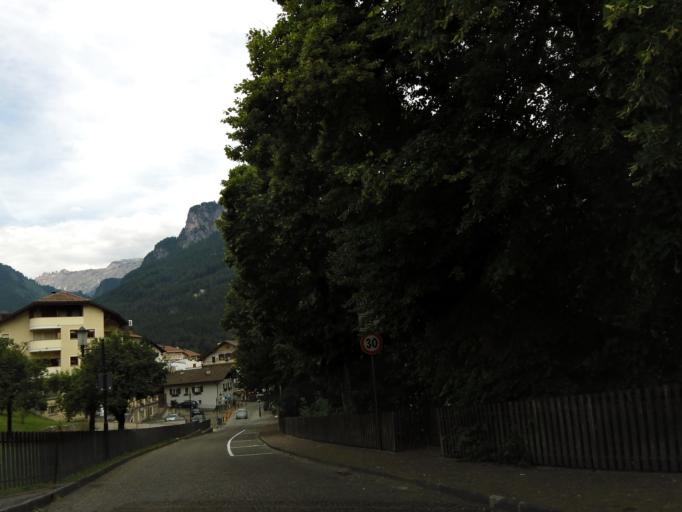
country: IT
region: Trentino-Alto Adige
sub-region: Bolzano
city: Siusi
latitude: 46.5467
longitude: 11.5592
